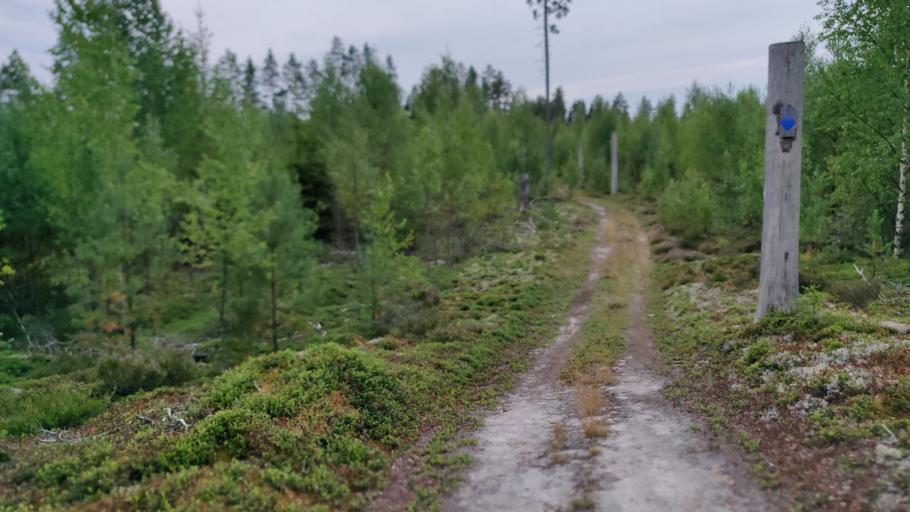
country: SE
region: Vaermland
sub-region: Hagfors Kommun
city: Hagfors
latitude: 60.0194
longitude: 13.5486
